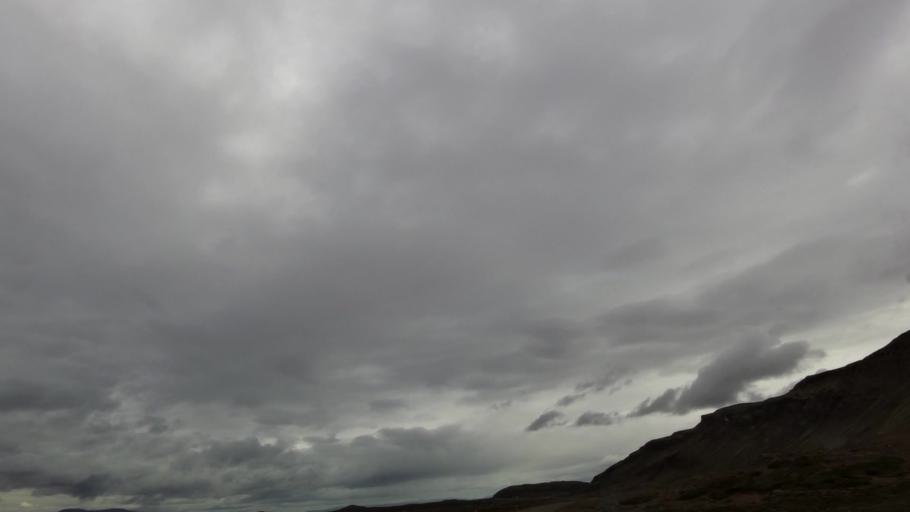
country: IS
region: West
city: Stykkisholmur
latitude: 65.0385
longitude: -22.4651
